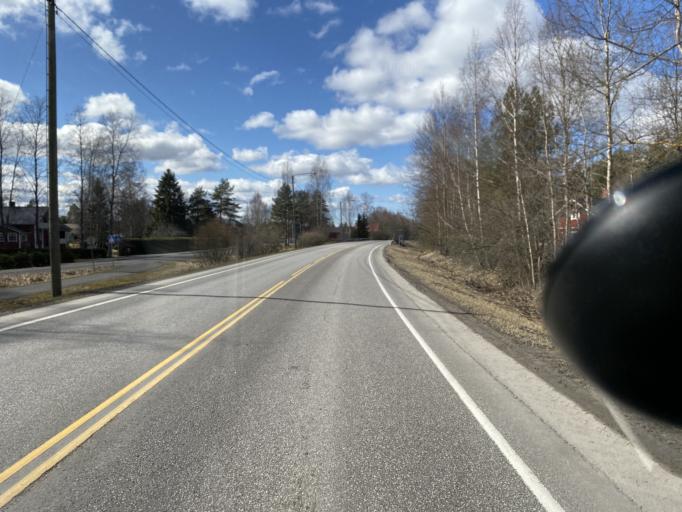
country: FI
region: Satakunta
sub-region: Rauma
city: Eura
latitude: 61.1317
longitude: 22.1548
